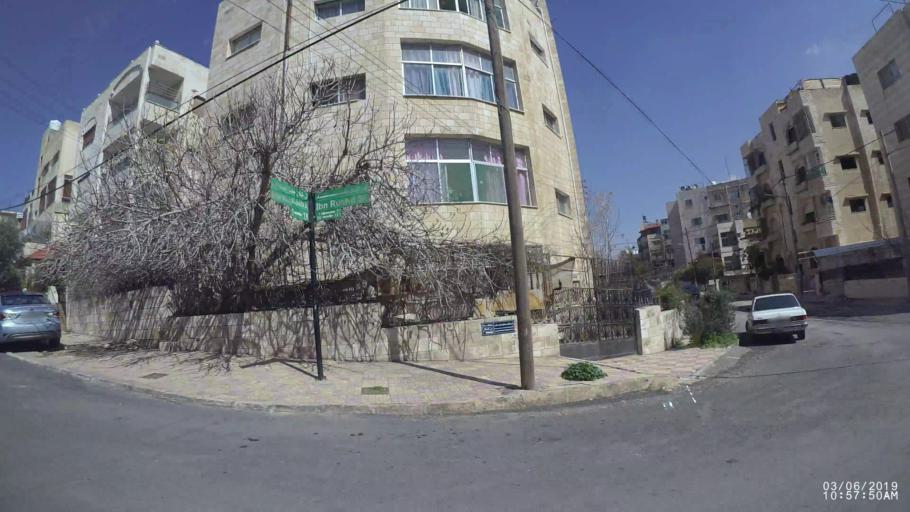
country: JO
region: Amman
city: Amman
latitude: 31.9749
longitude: 35.9874
